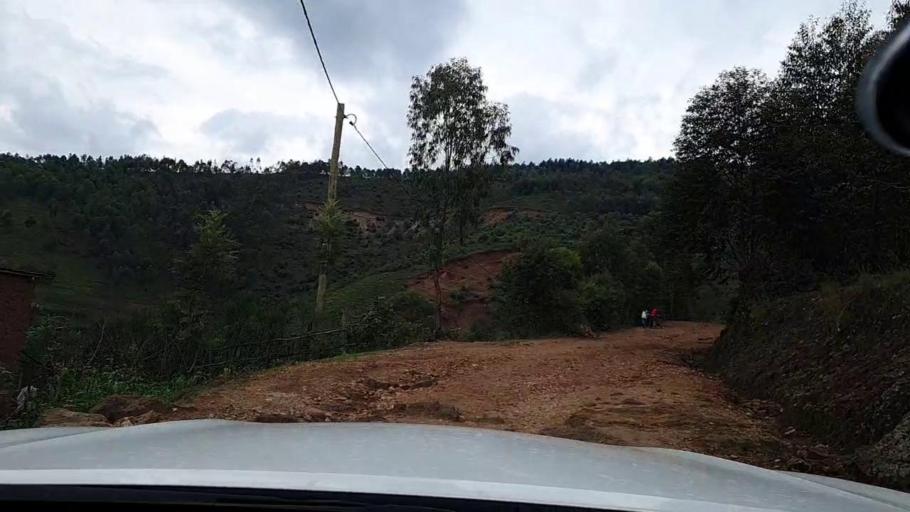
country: RW
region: Western Province
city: Kibuye
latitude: -2.1872
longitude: 29.2988
